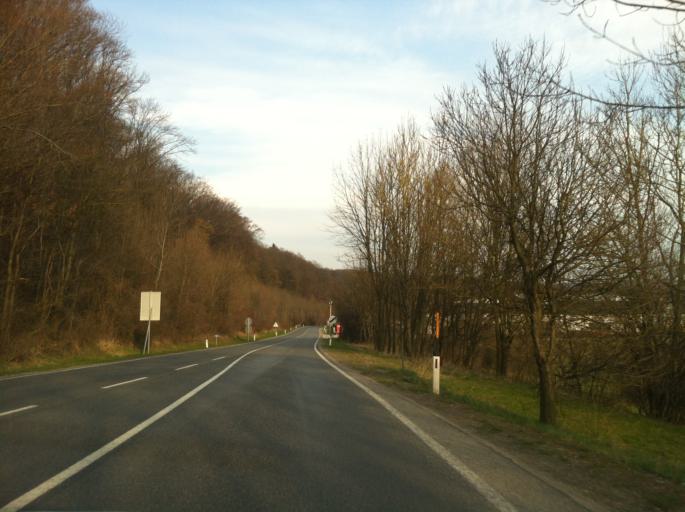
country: AT
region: Lower Austria
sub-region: Politischer Bezirk Wien-Umgebung
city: Gablitz
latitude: 48.2417
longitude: 16.1277
